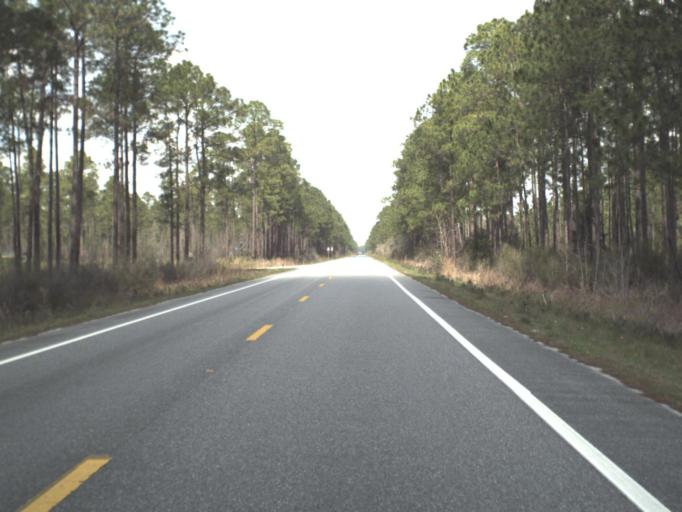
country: US
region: Florida
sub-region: Franklin County
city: Apalachicola
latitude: 29.8685
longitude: -84.9748
